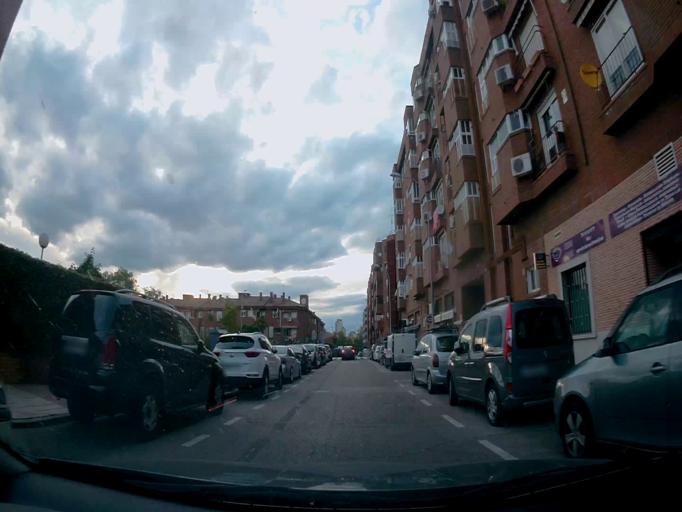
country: ES
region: Madrid
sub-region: Provincia de Madrid
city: Alcorcon
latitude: 40.3379
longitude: -3.8358
